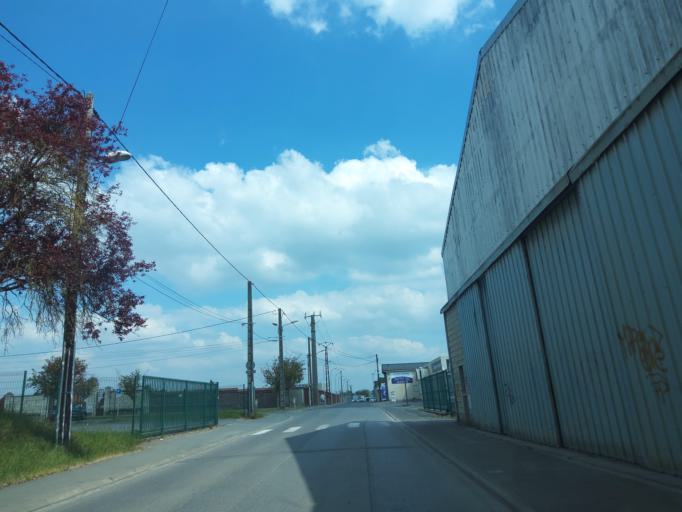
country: FR
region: Picardie
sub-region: Departement de l'Aisne
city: Laon
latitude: 49.5741
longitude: 3.6421
